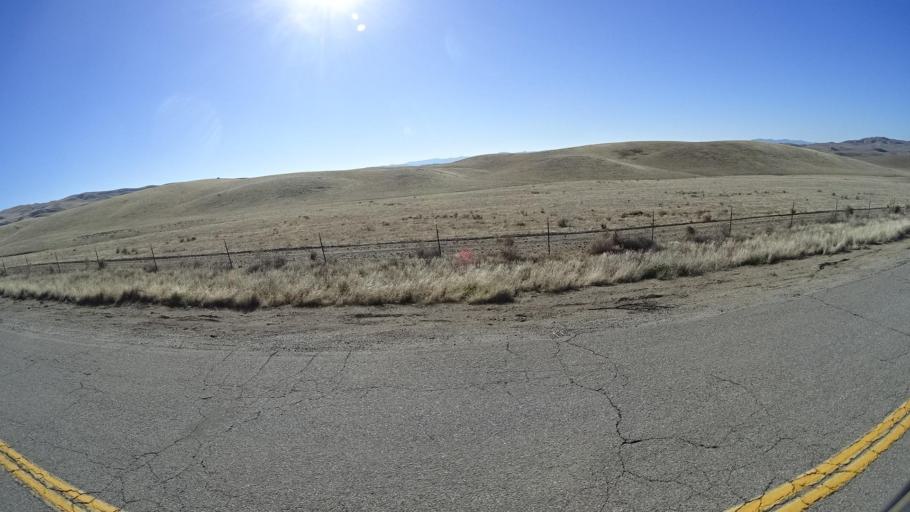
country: US
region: California
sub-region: Kern County
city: Maricopa
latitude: 34.9563
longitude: -119.4355
